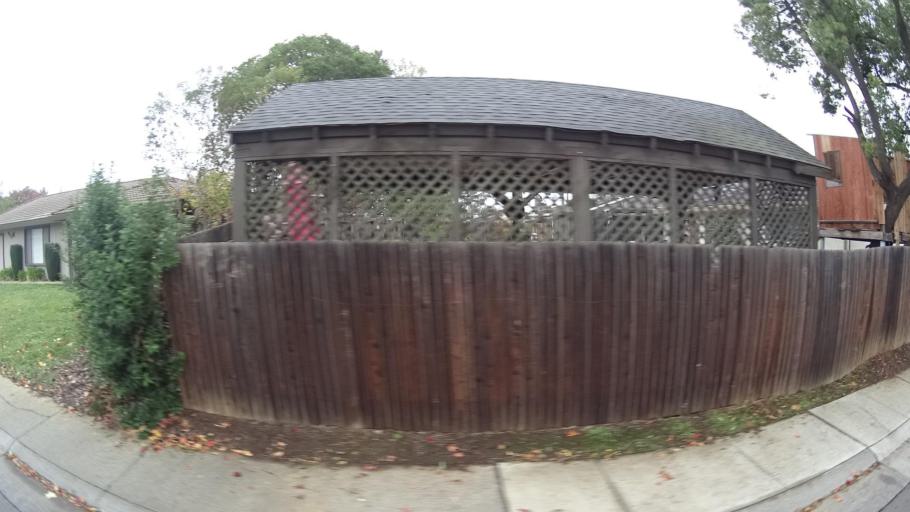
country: US
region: California
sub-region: Sacramento County
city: Elk Grove
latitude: 38.3969
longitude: -121.3691
